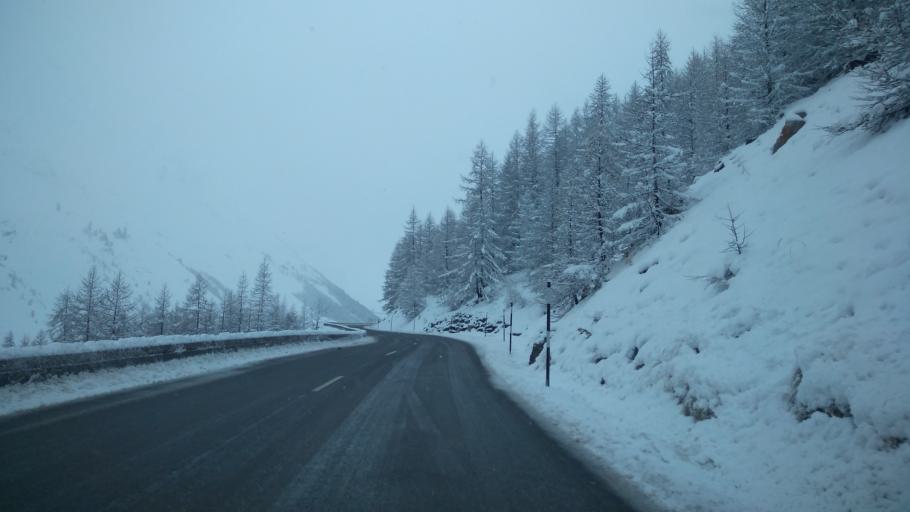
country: FR
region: Provence-Alpes-Cote d'Azur
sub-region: Departement des Hautes-Alpes
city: Le Monetier-les-Bains
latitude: 45.0246
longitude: 6.4538
